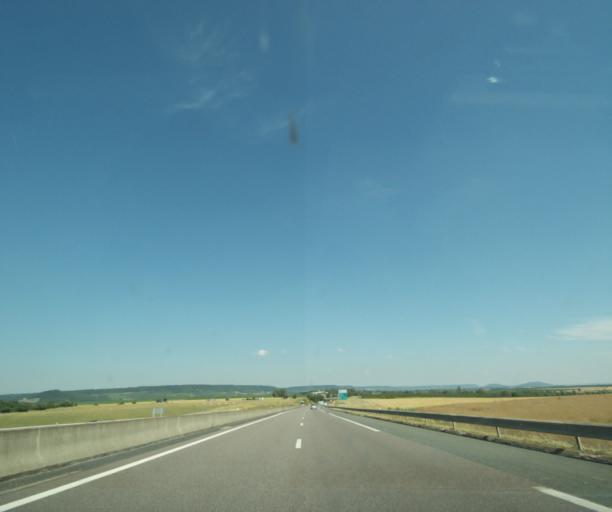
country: FR
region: Lorraine
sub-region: Departement de Meurthe-et-Moselle
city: Colombey-les-Belles
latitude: 48.5414
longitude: 5.9018
